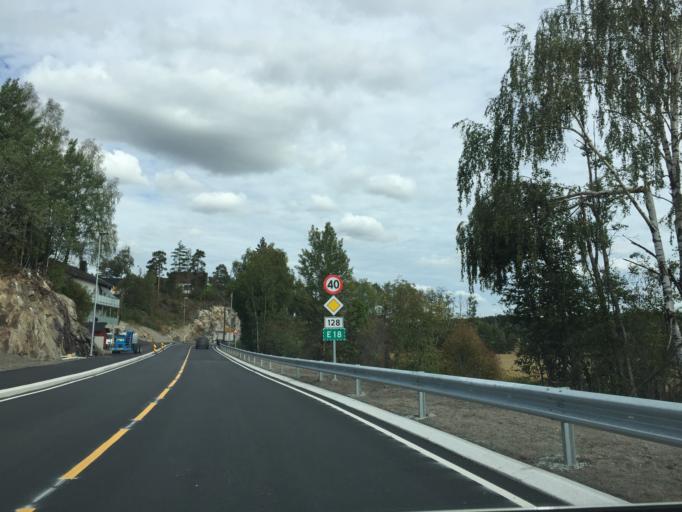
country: NO
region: Ostfold
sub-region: Hobol
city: Elvestad
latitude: 59.6232
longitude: 10.9517
